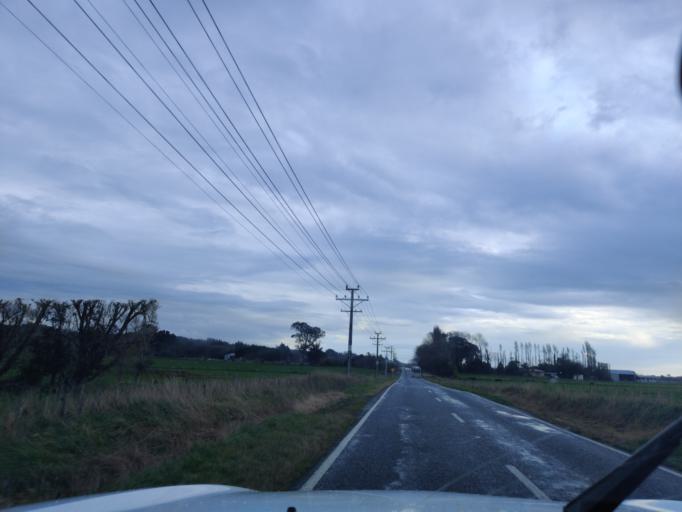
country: NZ
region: Manawatu-Wanganui
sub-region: Palmerston North City
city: Palmerston North
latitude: -40.3470
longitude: 175.7055
